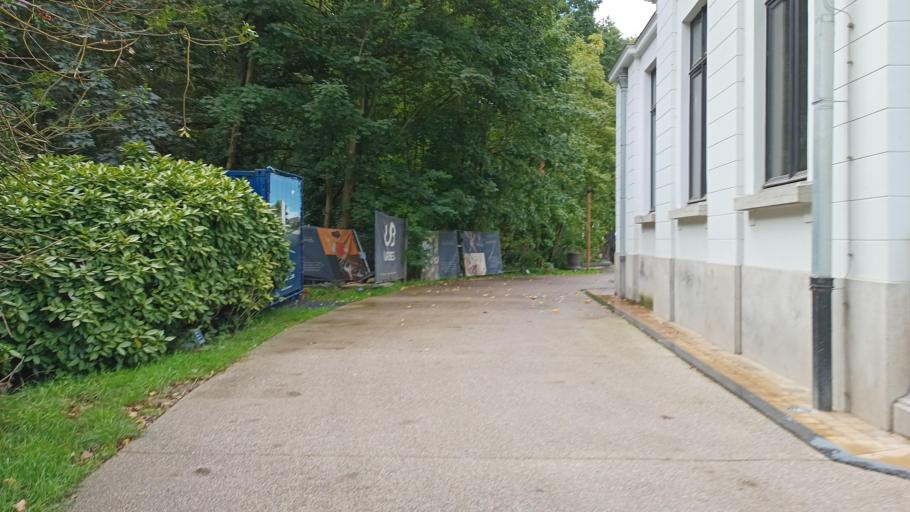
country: BE
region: Flanders
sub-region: Provincie West-Vlaanderen
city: Izegem
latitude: 50.9182
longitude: 3.2228
